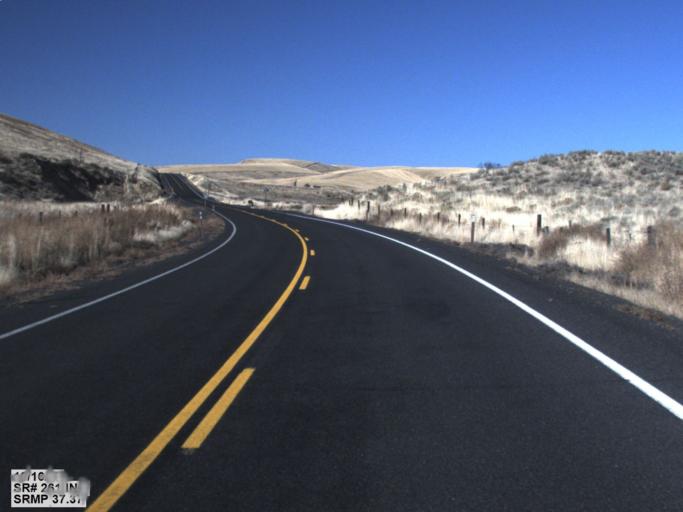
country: US
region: Washington
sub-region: Adams County
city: Ritzville
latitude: 46.7725
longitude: -118.2867
